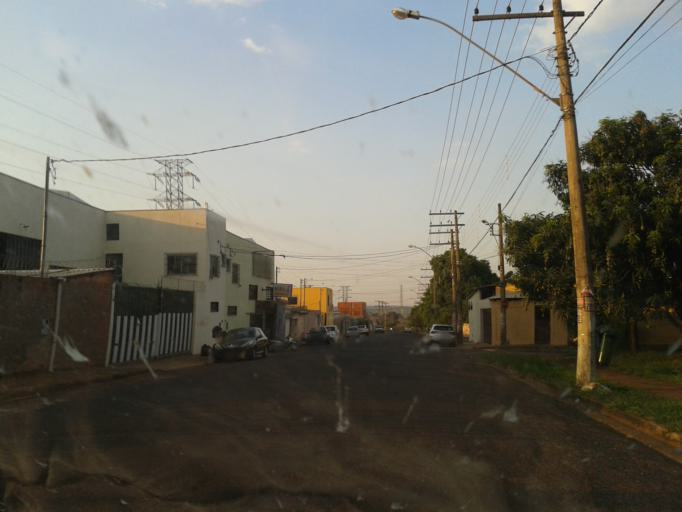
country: BR
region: Minas Gerais
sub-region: Uberlandia
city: Uberlandia
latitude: -18.9119
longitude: -48.3353
